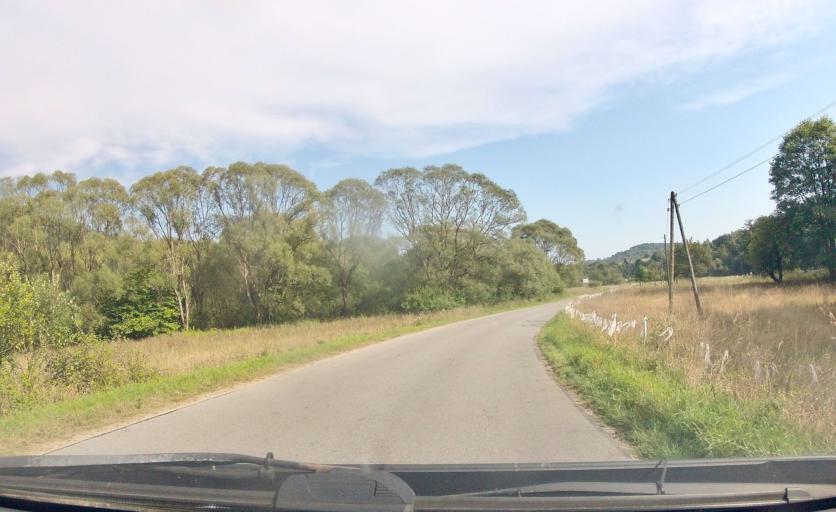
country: PL
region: Subcarpathian Voivodeship
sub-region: Powiat jasielski
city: Krempna
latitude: 49.5018
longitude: 21.5427
